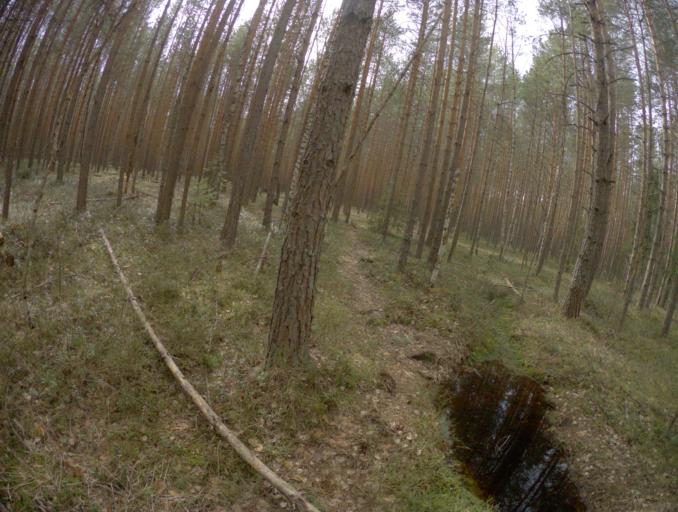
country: RU
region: Vladimir
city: Raduzhnyy
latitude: 55.9489
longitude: 40.2723
